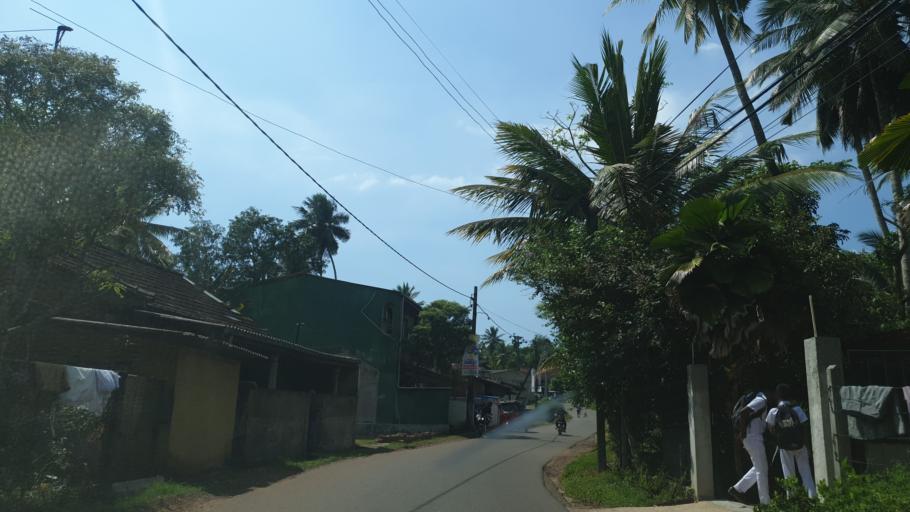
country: LK
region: Western
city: Panadura
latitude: 6.7221
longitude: 79.9585
